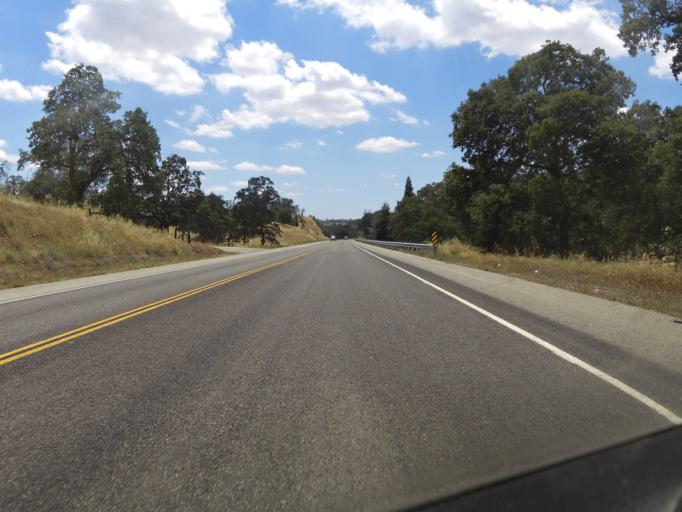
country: US
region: California
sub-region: Madera County
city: Yosemite Lakes
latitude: 37.1289
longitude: -119.6927
